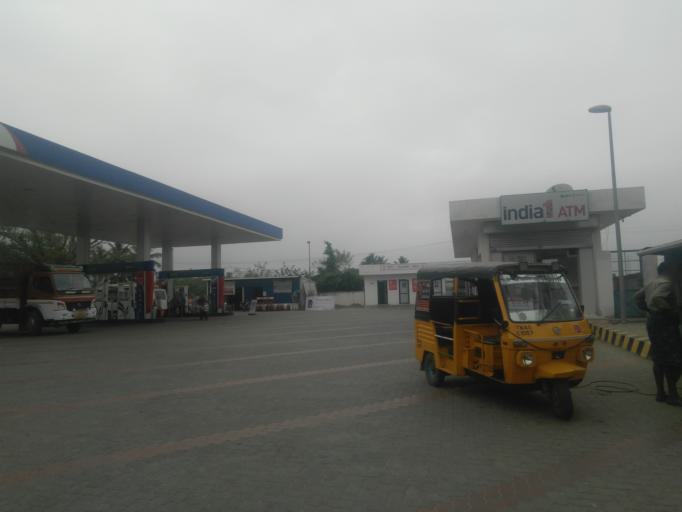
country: IN
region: Tamil Nadu
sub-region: Coimbatore
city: Karamadai
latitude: 11.2474
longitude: 76.9566
